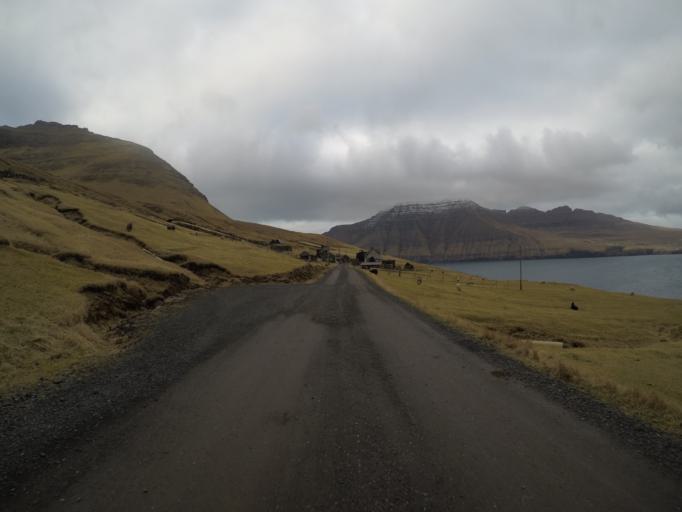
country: FO
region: Nordoyar
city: Klaksvik
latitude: 62.3498
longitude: -6.5823
